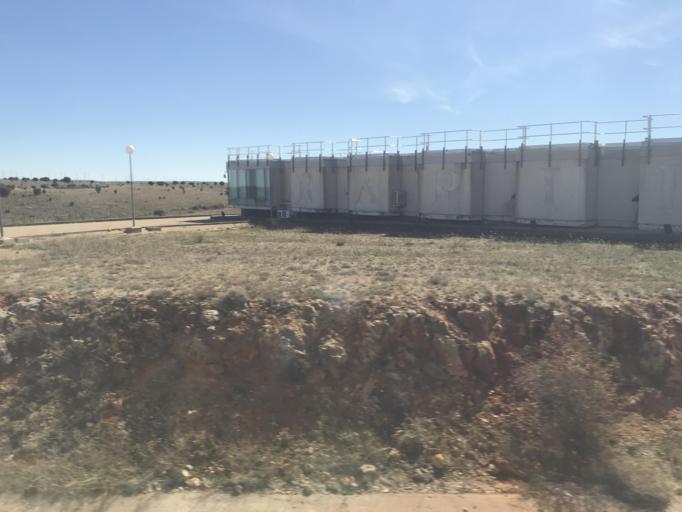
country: ES
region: Castille-La Mancha
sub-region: Provincia de Guadalajara
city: Anguita
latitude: 41.1204
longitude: -2.3495
